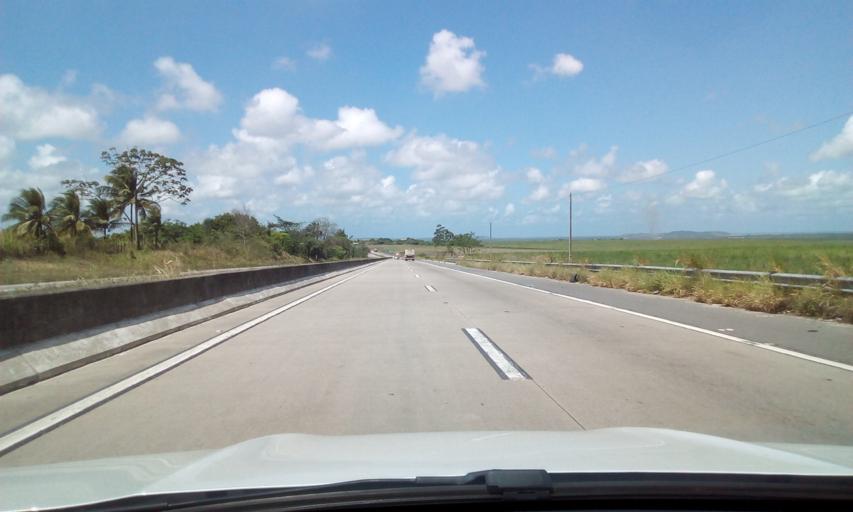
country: BR
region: Pernambuco
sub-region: Itapissuma
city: Itapissuma
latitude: -7.7123
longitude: -34.9324
